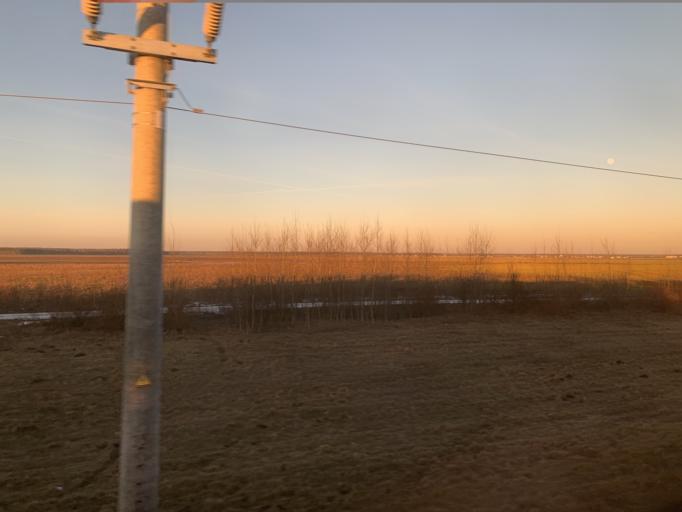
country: BY
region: Minsk
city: Nasilava
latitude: 54.3179
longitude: 26.7837
